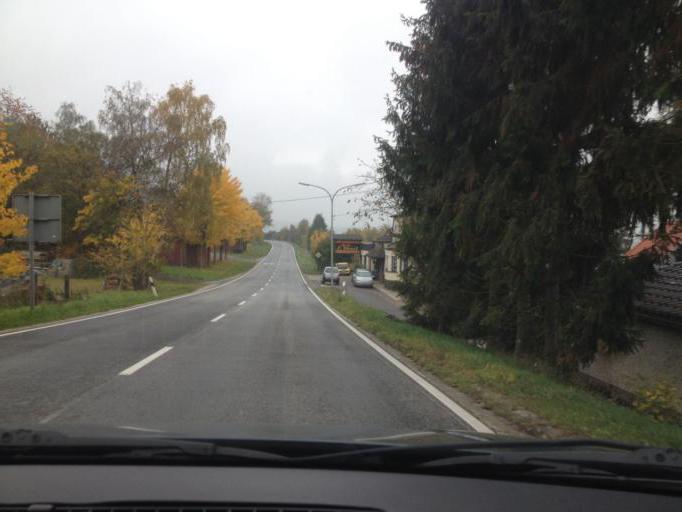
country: DE
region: Saarland
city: Tholey
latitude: 49.4802
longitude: 7.0422
